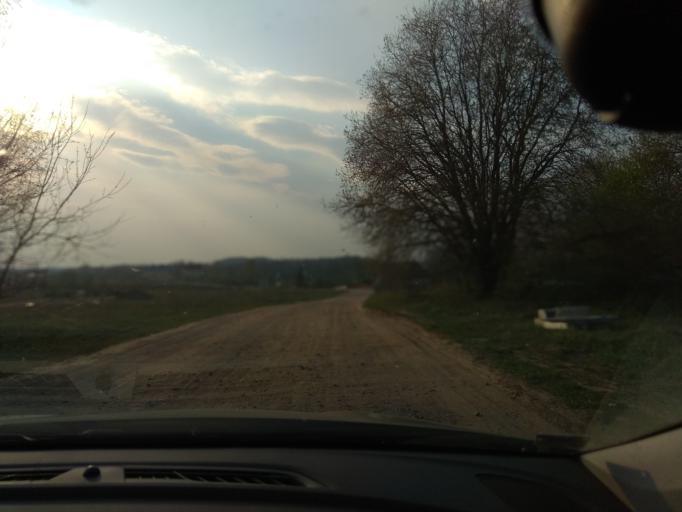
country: LT
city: Baltoji Voke
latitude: 54.5943
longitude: 25.1668
